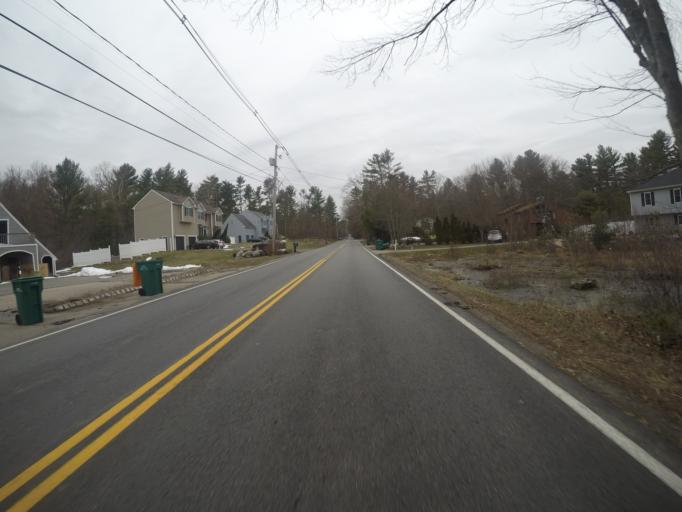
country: US
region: Massachusetts
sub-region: Bristol County
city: Easton
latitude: 42.0197
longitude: -71.1074
